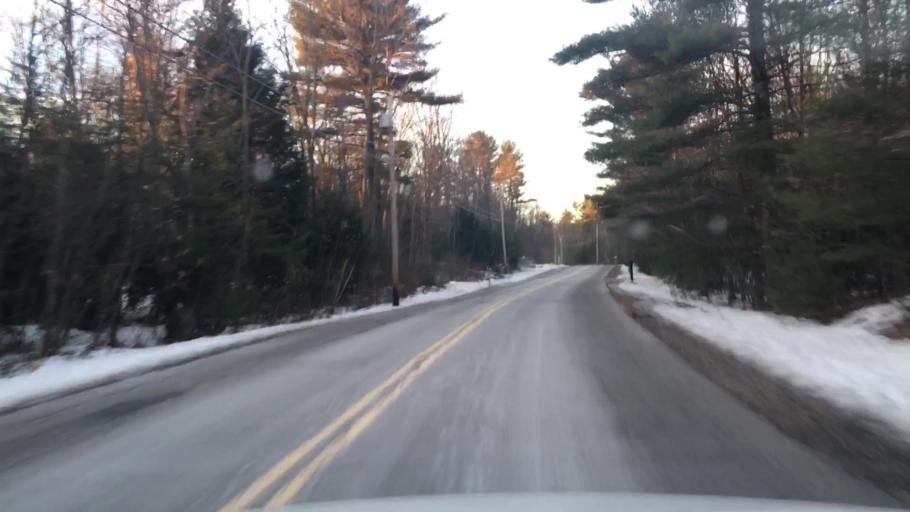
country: US
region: Maine
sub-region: York County
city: Lebanon
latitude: 43.3457
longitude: -70.8657
